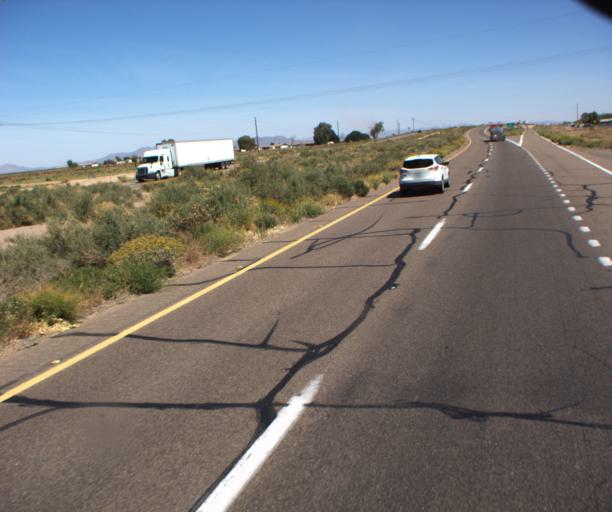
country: US
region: Arizona
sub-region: Maricopa County
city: Gila Bend
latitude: 32.9202
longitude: -112.8936
